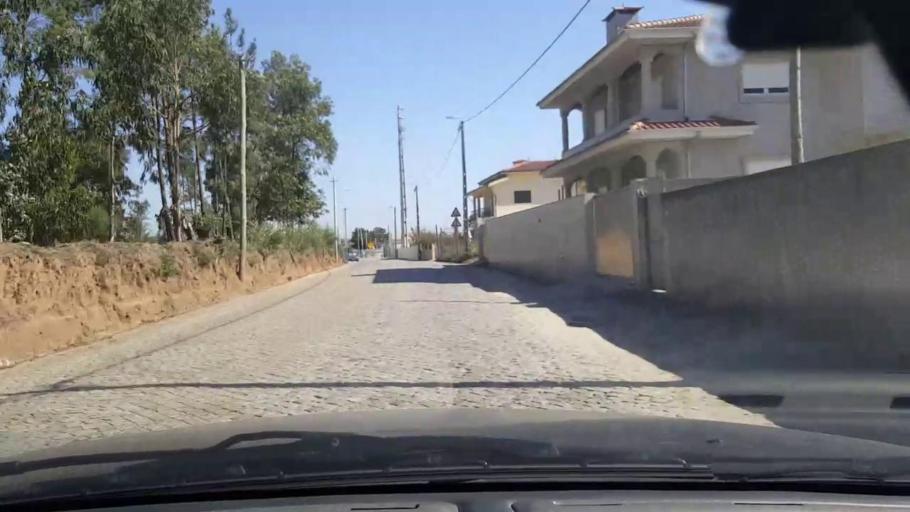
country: PT
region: Porto
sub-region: Matosinhos
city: Lavra
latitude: 41.2949
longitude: -8.7016
